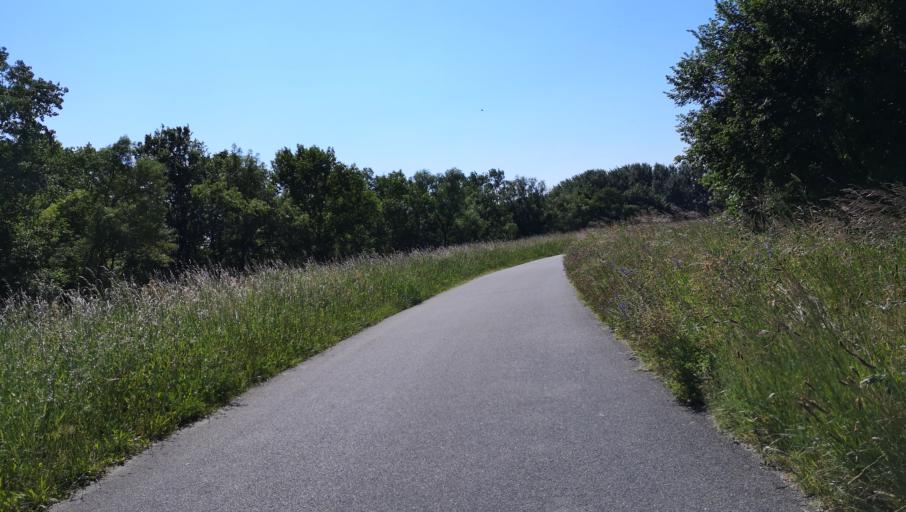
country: FR
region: Centre
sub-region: Departement du Loiret
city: Mareau-aux-Pres
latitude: 47.8619
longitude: 1.8018
